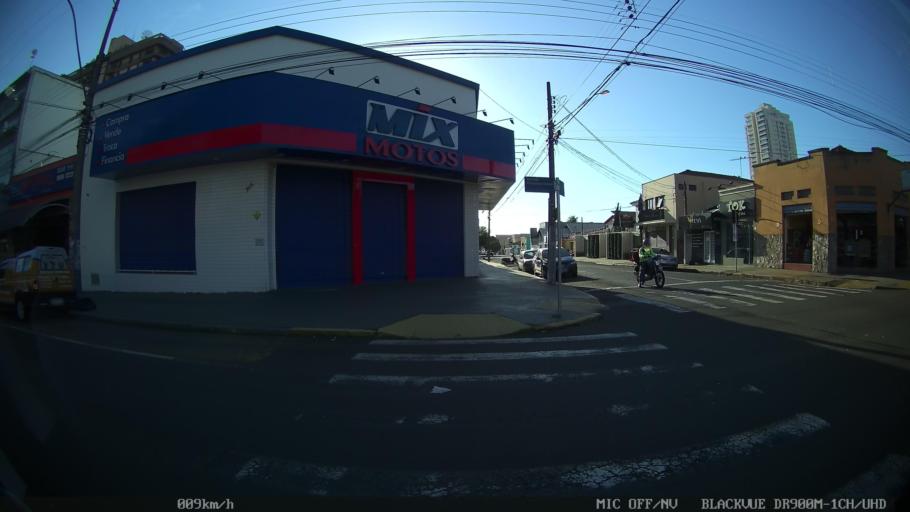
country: BR
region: Sao Paulo
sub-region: Franca
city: Franca
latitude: -20.5316
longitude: -47.3958
